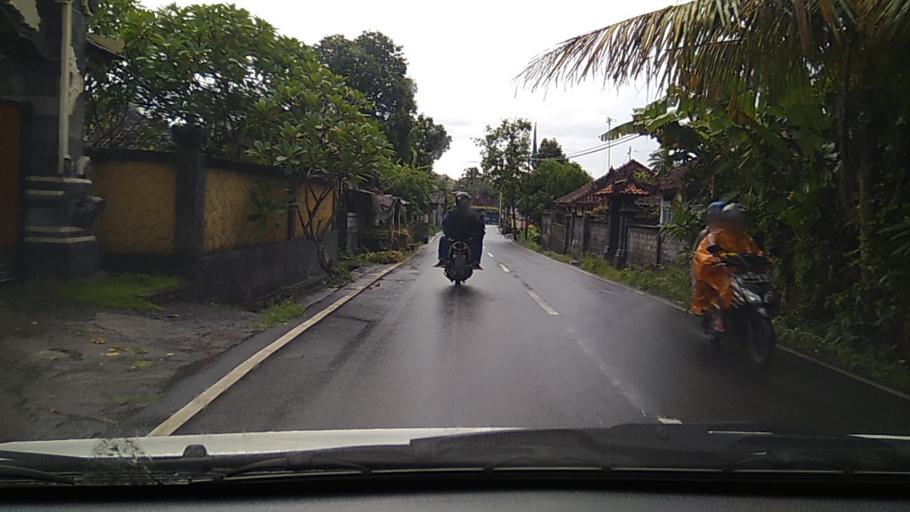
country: ID
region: Bali
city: Banjar Danginsema
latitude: -8.4632
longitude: 115.6241
